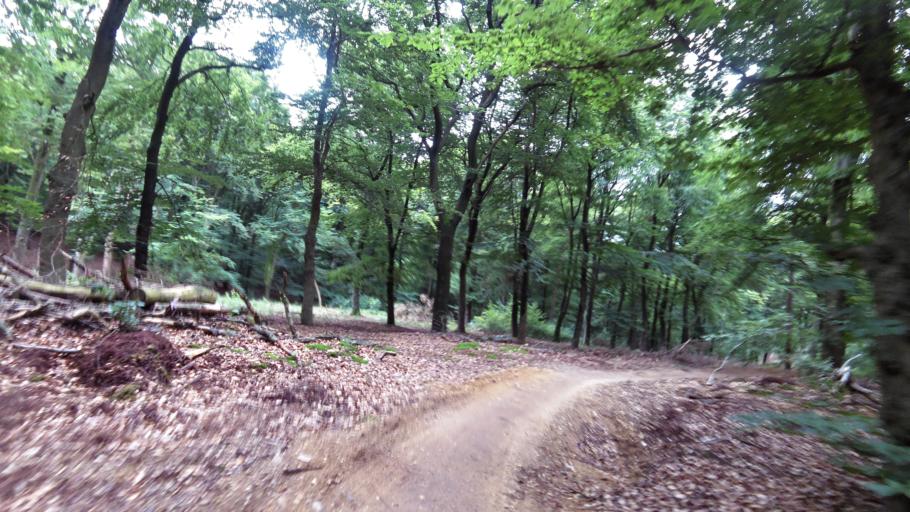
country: NL
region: Utrecht
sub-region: Gemeente Utrechtse Heuvelrug
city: Amerongen
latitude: 52.0053
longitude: 5.4819
